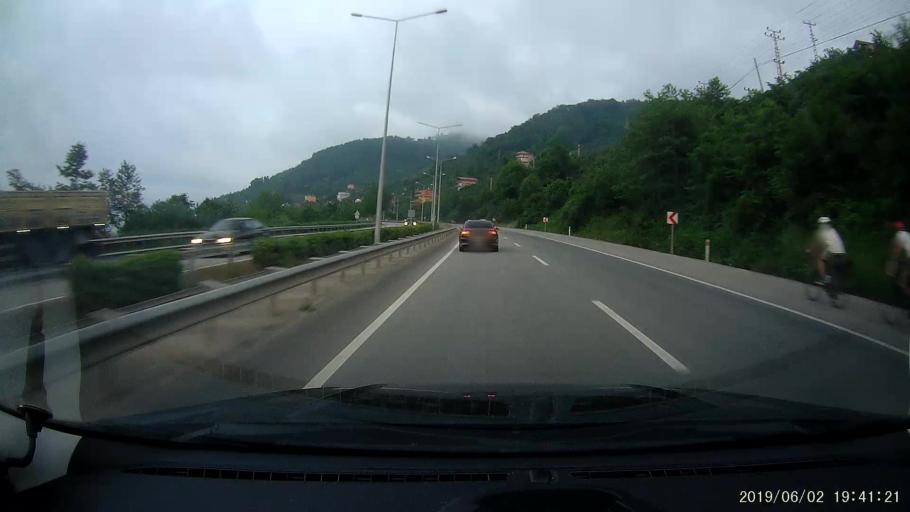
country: TR
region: Giresun
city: Kesap
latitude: 40.9142
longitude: 38.4781
